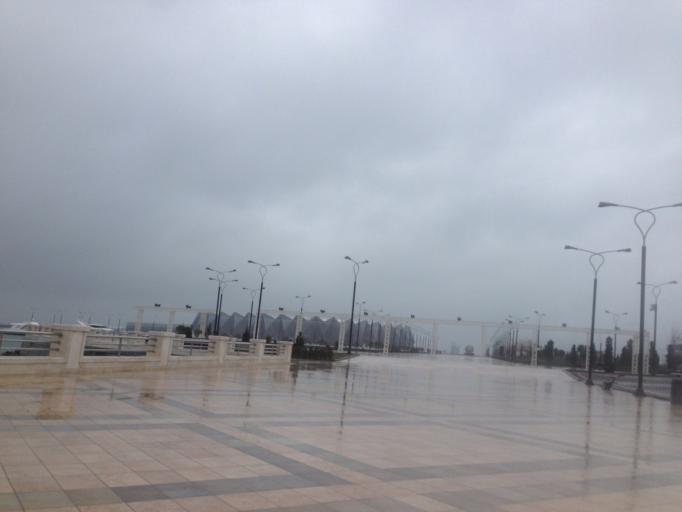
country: AZ
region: Baki
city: Badamdar
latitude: 40.3482
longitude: 49.8455
